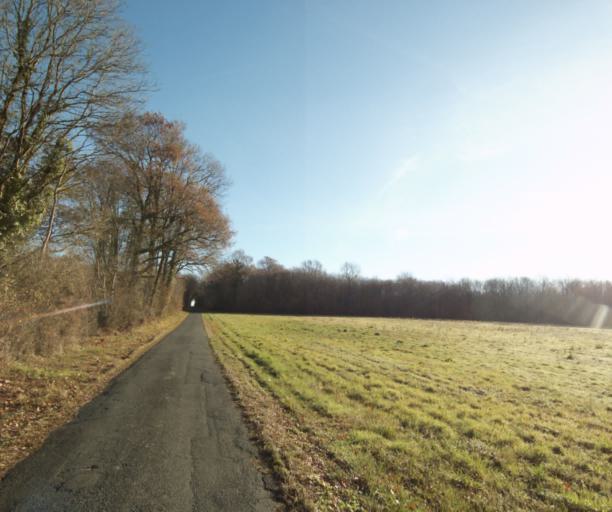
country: FR
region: Poitou-Charentes
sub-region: Departement de la Charente-Maritime
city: Cherac
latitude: 45.7390
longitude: -0.4661
